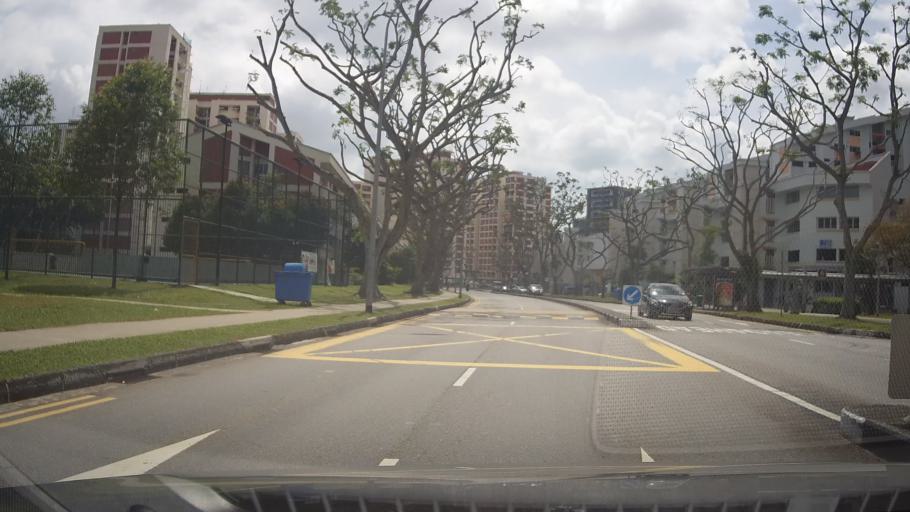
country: SG
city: Singapore
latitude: 1.3357
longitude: 103.8664
